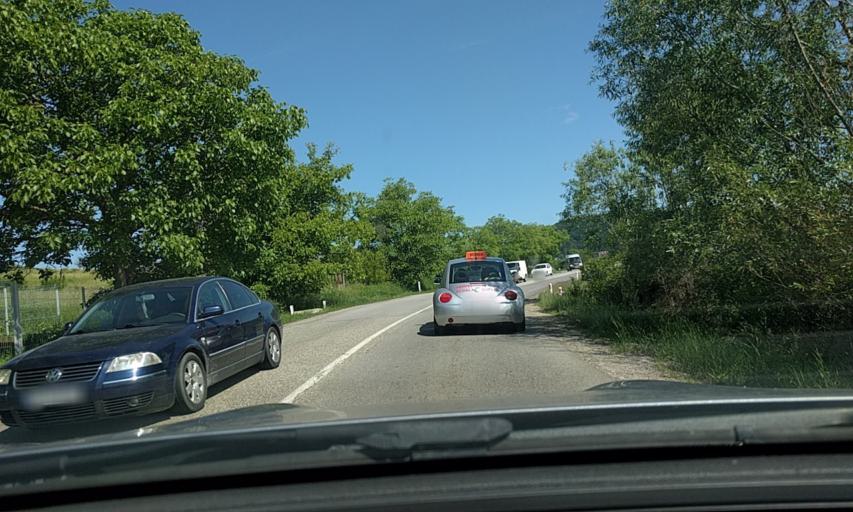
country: RO
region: Bistrita-Nasaud
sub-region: Municipiul Bistrita
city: Unirea
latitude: 47.1741
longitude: 24.4938
